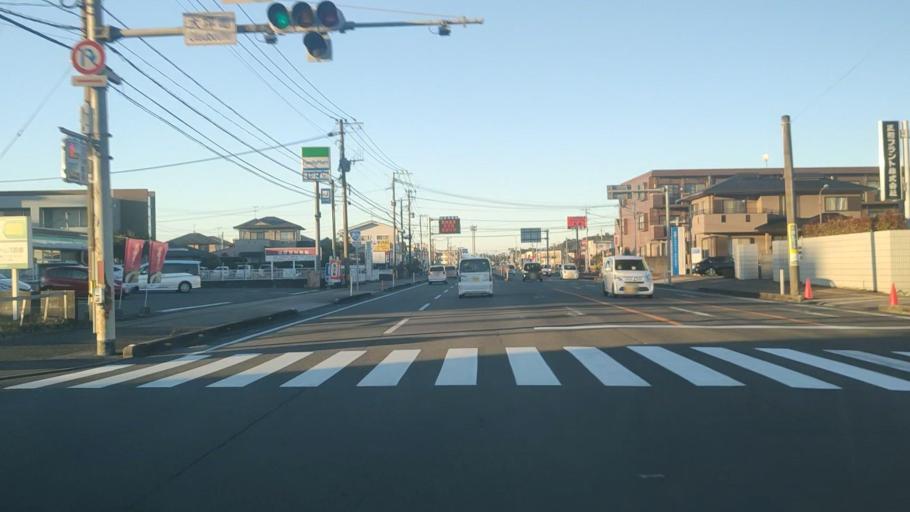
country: JP
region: Miyazaki
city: Miyazaki-shi
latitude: 31.8961
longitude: 131.4067
